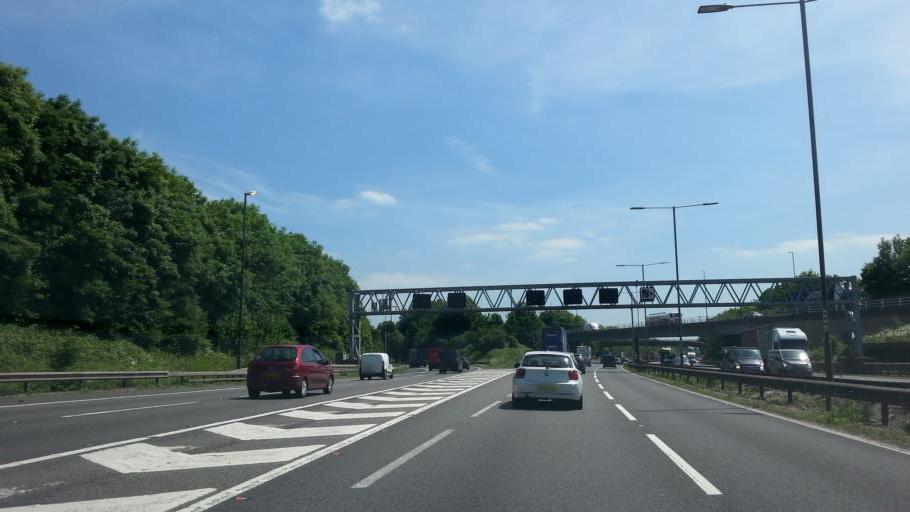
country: GB
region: England
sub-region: Warwickshire
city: Water Orton
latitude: 52.5097
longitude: -1.7449
